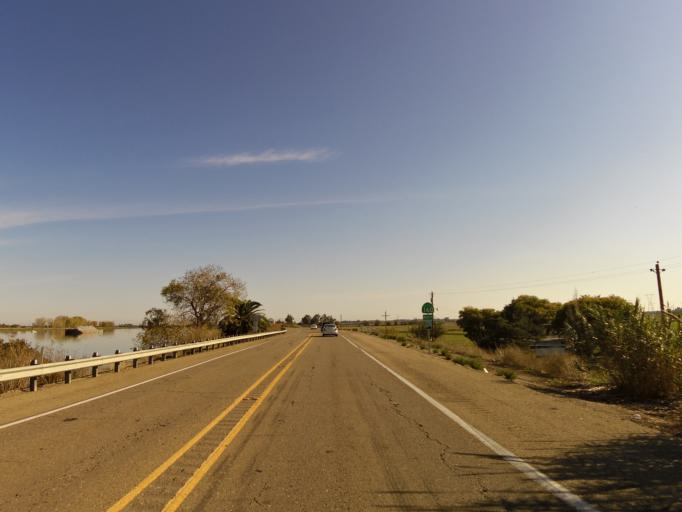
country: US
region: California
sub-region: Contra Costa County
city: Oakley
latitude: 38.0801
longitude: -121.7287
